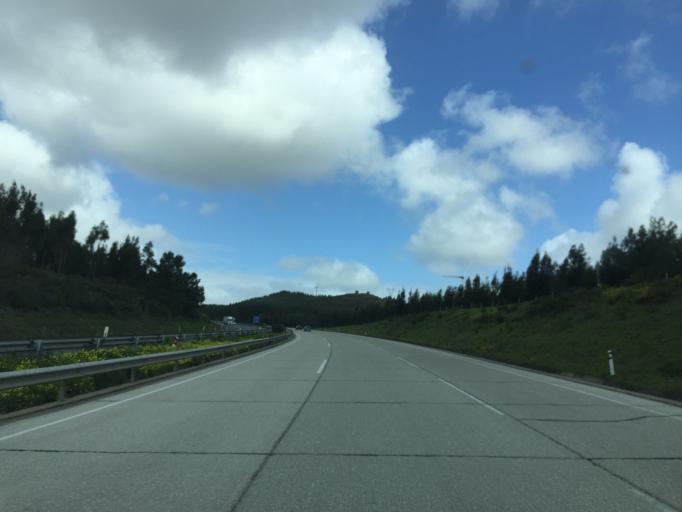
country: PT
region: Lisbon
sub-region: Sobral de Monte Agraco
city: Sobral de Monte Agraco
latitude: 39.0114
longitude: -9.2120
